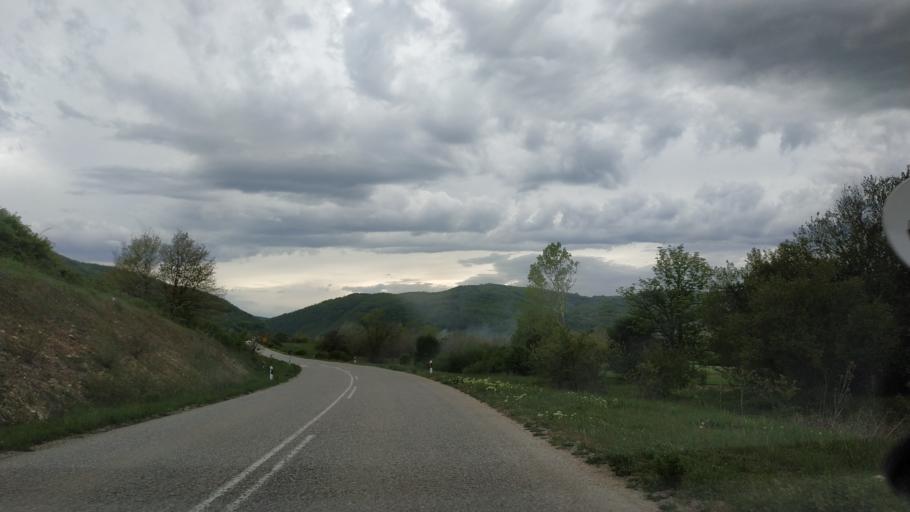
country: RS
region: Central Serbia
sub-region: Zajecarski Okrug
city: Soko Banja
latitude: 43.6545
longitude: 21.7798
